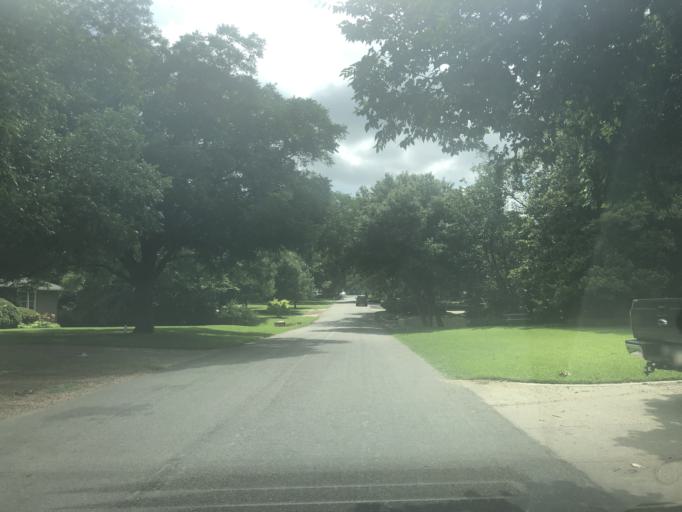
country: US
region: Texas
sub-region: Dallas County
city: University Park
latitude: 32.8676
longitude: -96.8377
